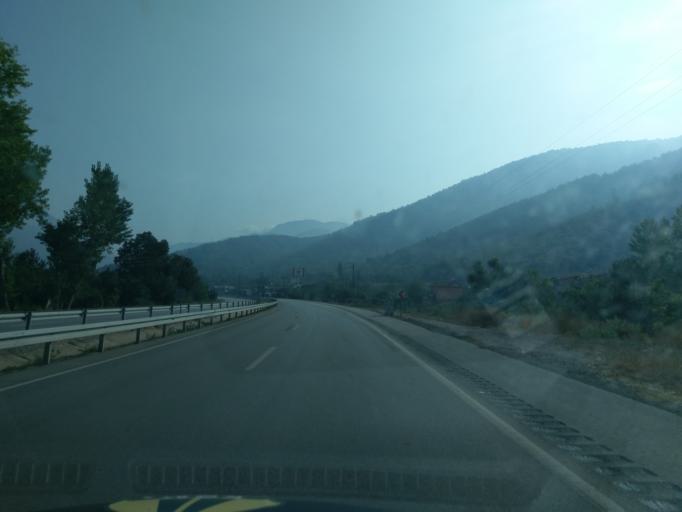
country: TR
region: Amasya
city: Akdag
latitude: 40.6853
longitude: 35.9080
